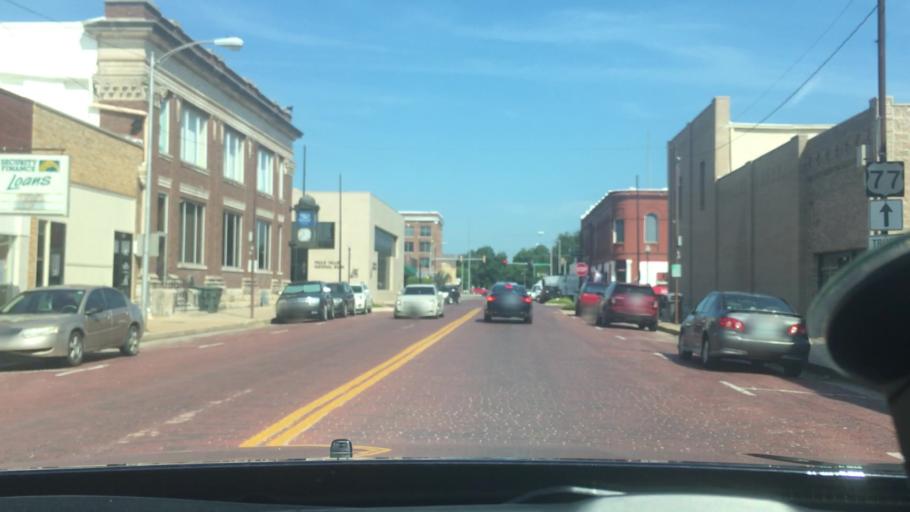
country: US
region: Oklahoma
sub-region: Garvin County
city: Pauls Valley
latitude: 34.7402
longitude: -97.2192
